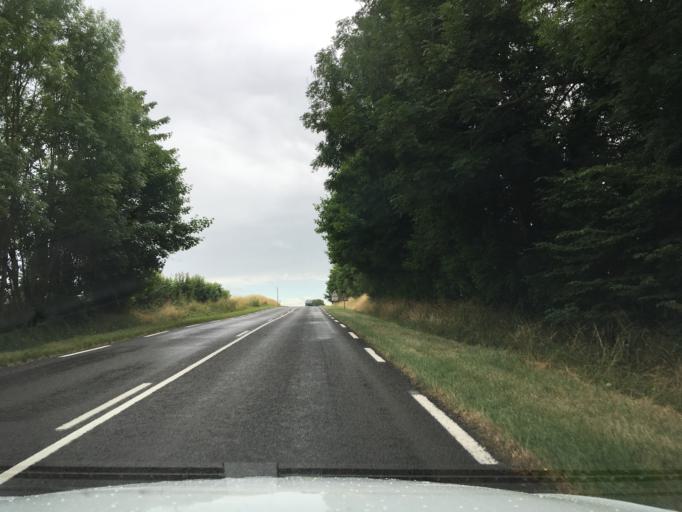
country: FR
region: Picardie
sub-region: Departement de l'Aisne
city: Guise
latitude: 49.9092
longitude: 3.6588
